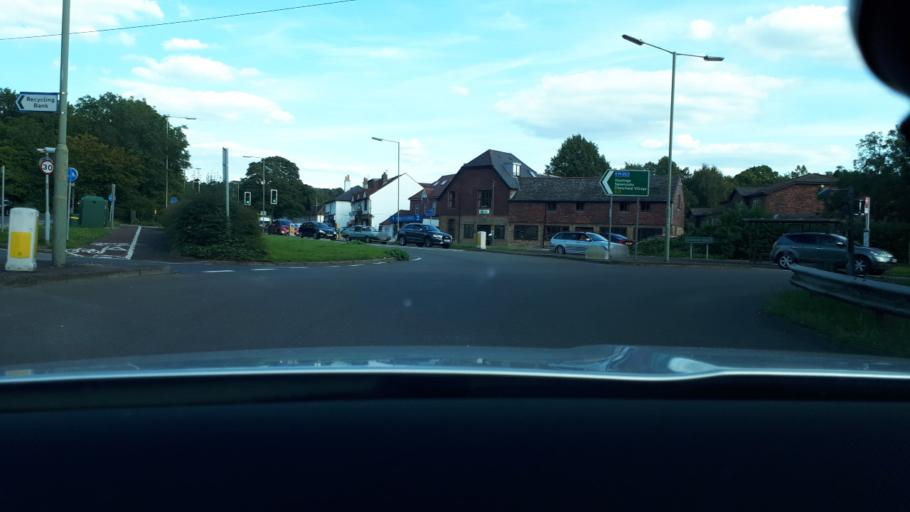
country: GB
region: England
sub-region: Kent
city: Halstead
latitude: 51.3448
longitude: 0.1111
